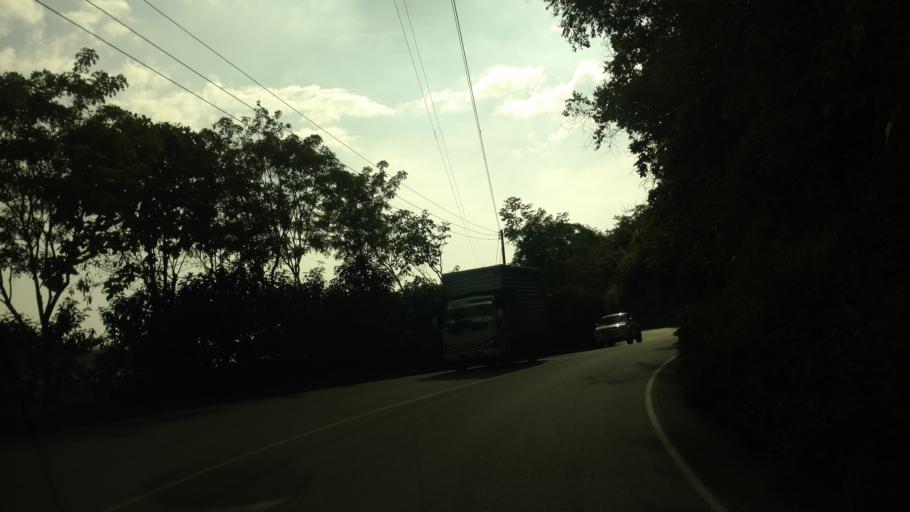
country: CO
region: Caldas
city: Neira
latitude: 5.1381
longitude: -75.4973
